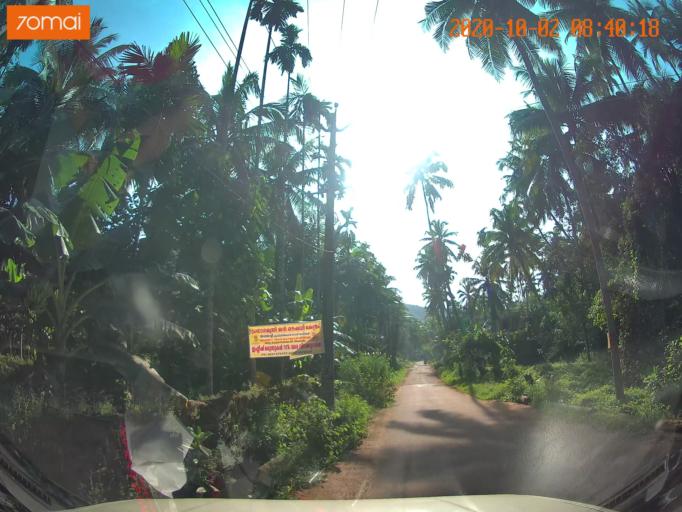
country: IN
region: Kerala
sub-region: Kozhikode
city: Naduvannur
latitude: 11.4099
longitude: 75.7654
